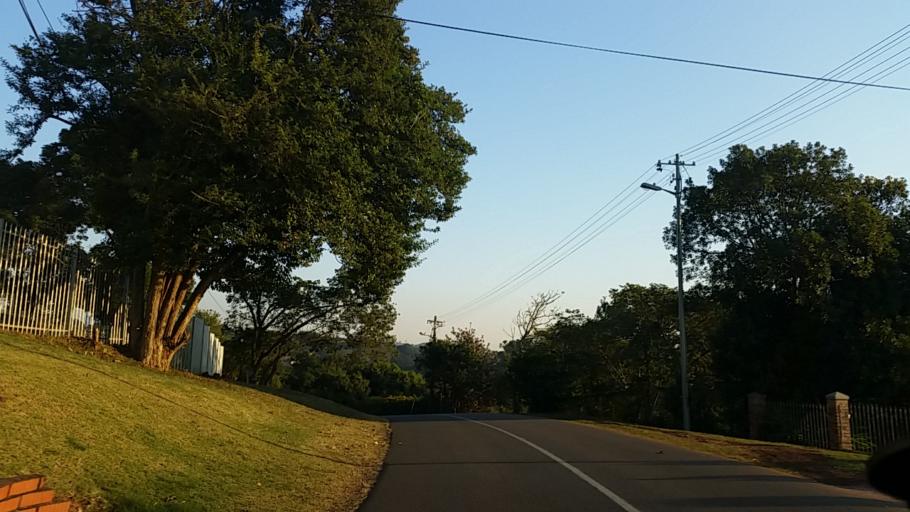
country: ZA
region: KwaZulu-Natal
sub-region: eThekwini Metropolitan Municipality
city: Berea
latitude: -29.8448
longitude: 30.9118
